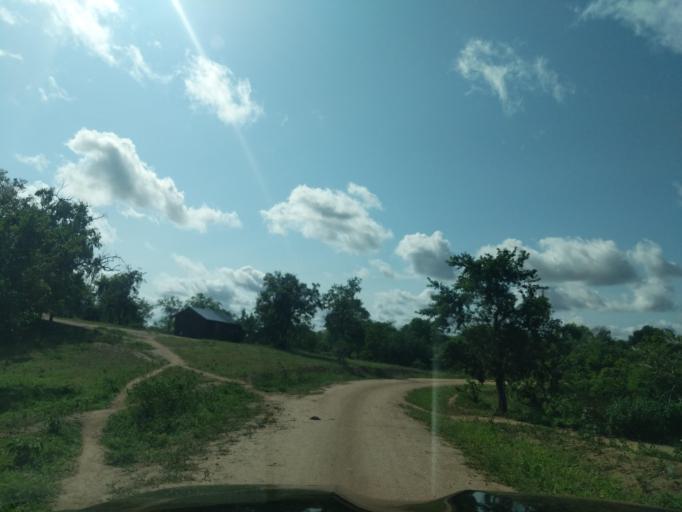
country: TZ
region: Tanga
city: Muheza
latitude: -5.4186
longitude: 38.6467
